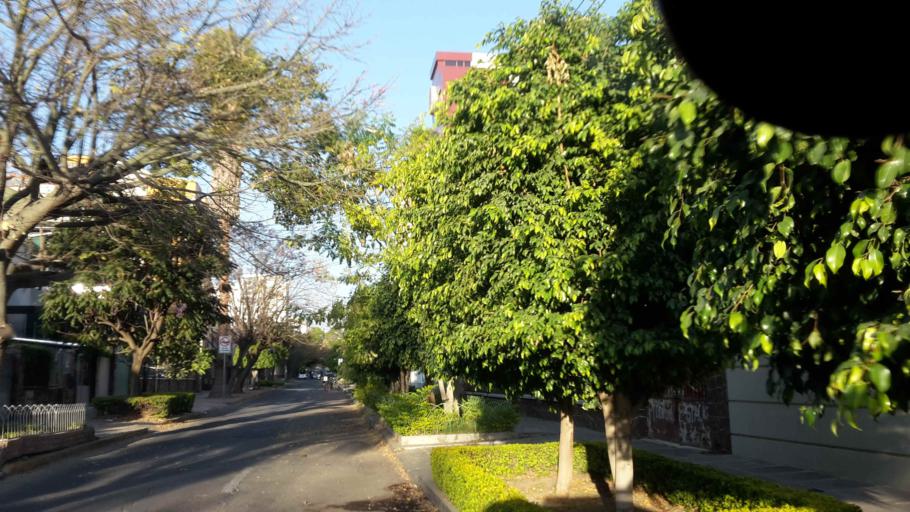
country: BO
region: Cochabamba
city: Cochabamba
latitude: -17.3716
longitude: -66.1620
